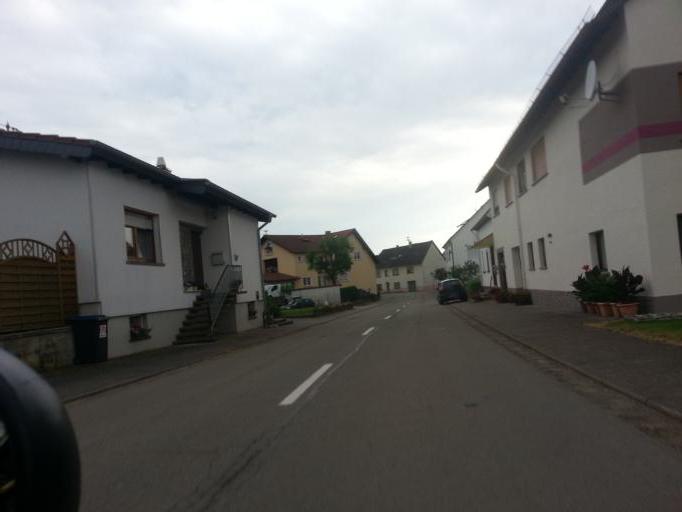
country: DE
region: Rheinland-Pfalz
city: Gimbweiler
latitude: 49.5688
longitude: 7.1767
